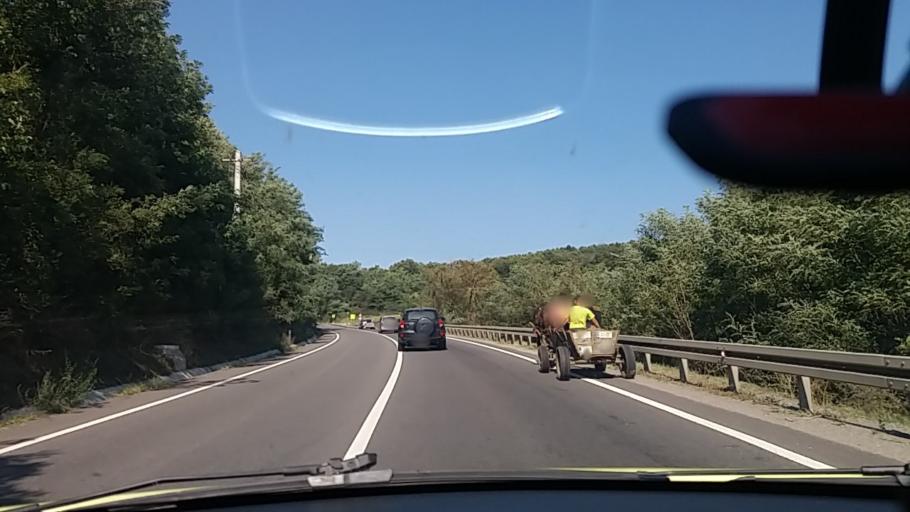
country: RO
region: Sibiu
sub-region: Comuna Slimnic
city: Slimnic
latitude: 45.9349
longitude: 24.1717
